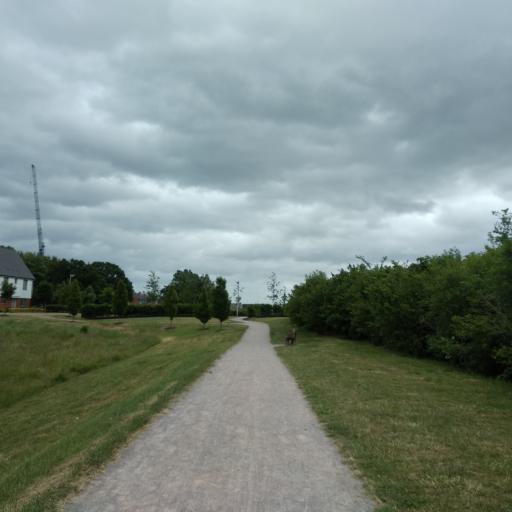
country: GB
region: England
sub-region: Kent
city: Ashford
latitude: 51.1570
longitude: 0.8505
